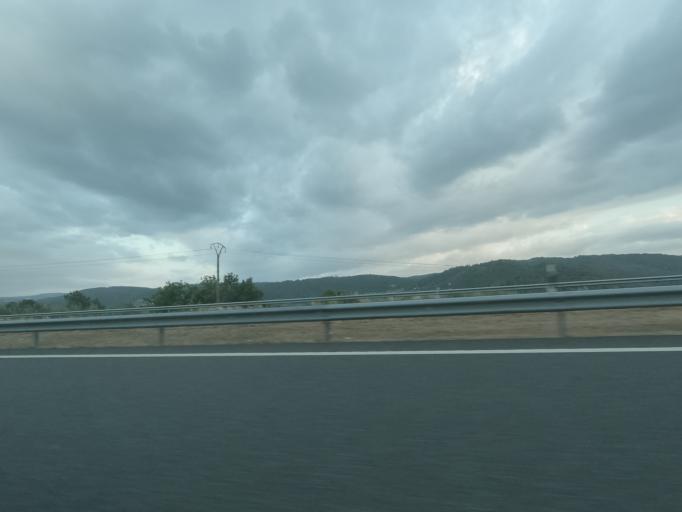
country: ES
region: Galicia
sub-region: Provincia de Ourense
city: Castrelo de Mino
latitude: 42.3324
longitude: -8.0365
